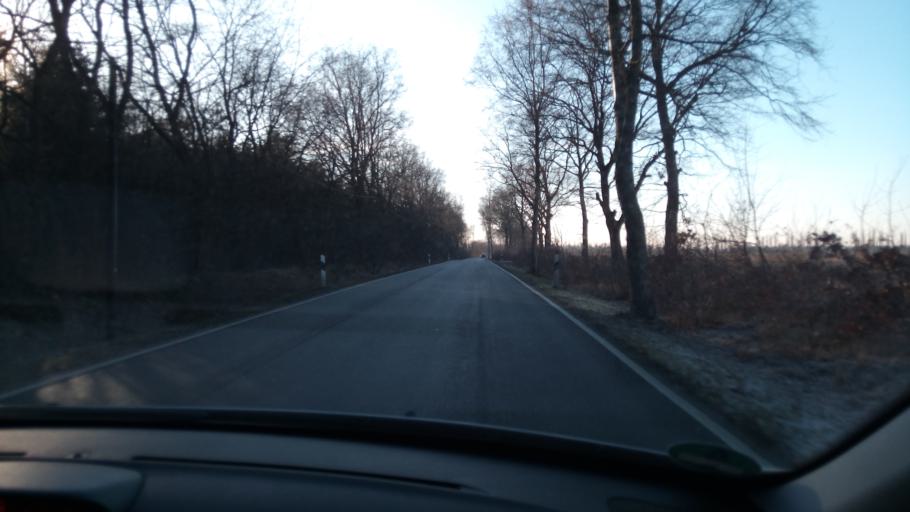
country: DE
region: Schleswig-Holstein
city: Brothen
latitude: 53.4942
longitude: 10.6710
